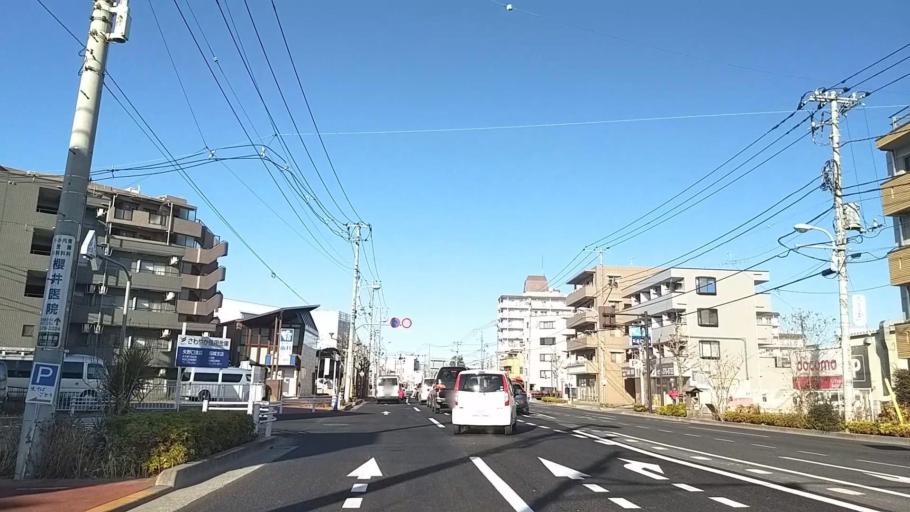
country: JP
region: Tokyo
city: Chofugaoka
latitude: 35.6407
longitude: 139.5197
